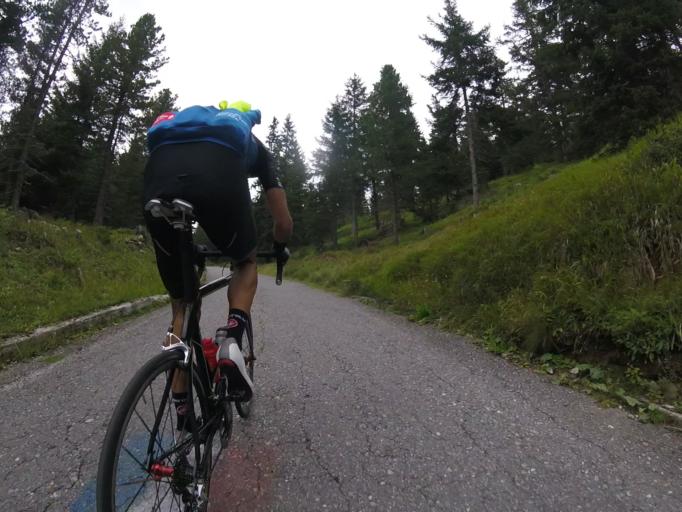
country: IT
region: Lombardy
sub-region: Provincia di Sondrio
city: Mazzo di Valtellina
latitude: 46.2456
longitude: 10.2908
